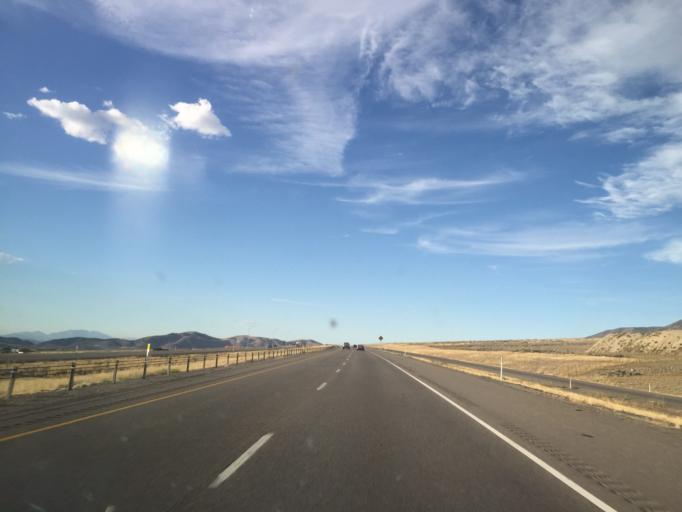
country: US
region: Utah
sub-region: Juab County
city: Mona
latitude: 39.8219
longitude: -111.8333
